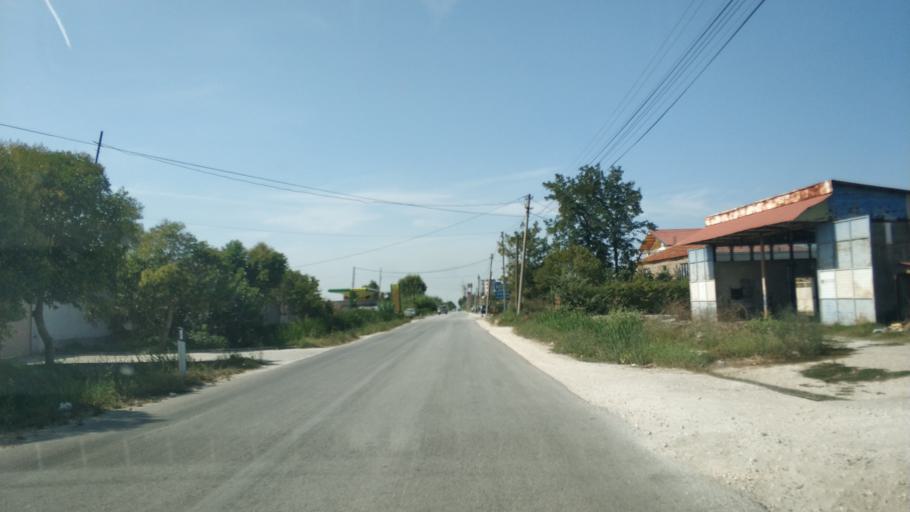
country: AL
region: Fier
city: Fier
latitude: 40.7323
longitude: 19.5351
